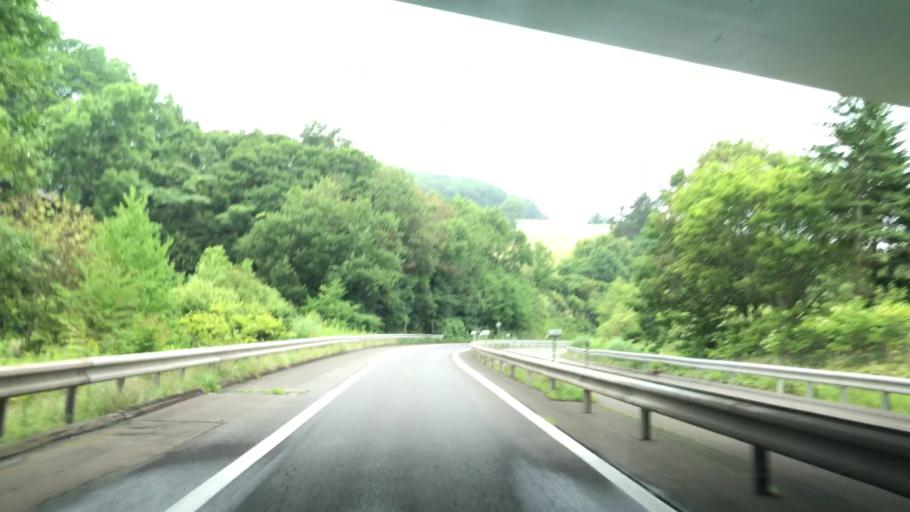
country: JP
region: Hokkaido
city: Muroran
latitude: 42.3989
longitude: 141.0803
